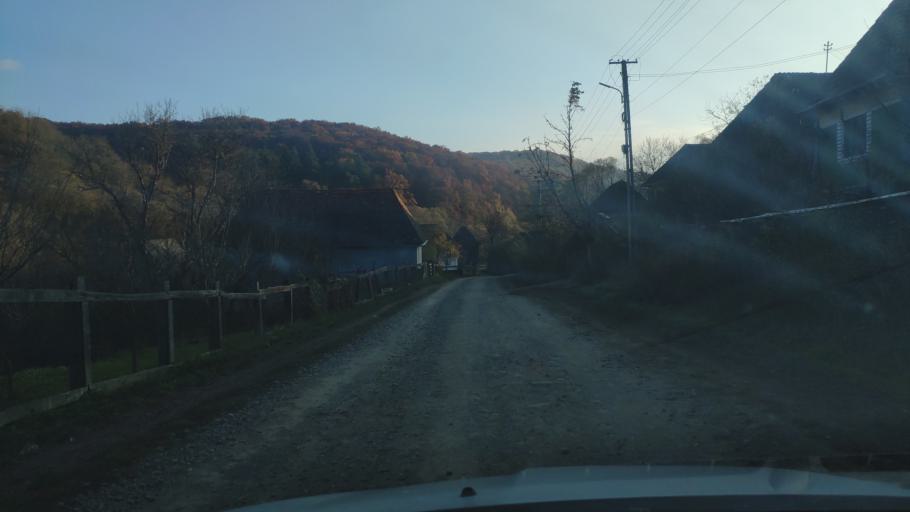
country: RO
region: Mures
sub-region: Comuna Ghindari
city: Ghindari
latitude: 46.5235
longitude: 24.9152
